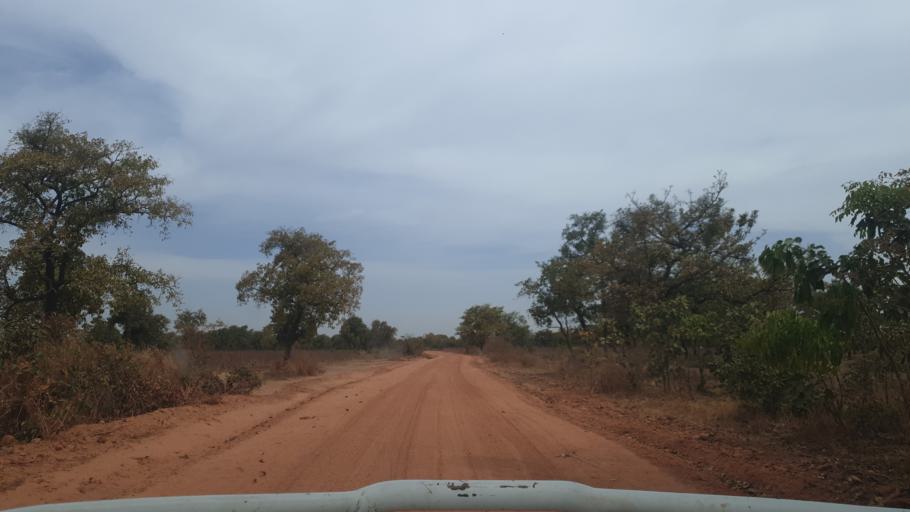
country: ML
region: Sikasso
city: Yorosso
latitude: 12.2214
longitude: -4.7539
